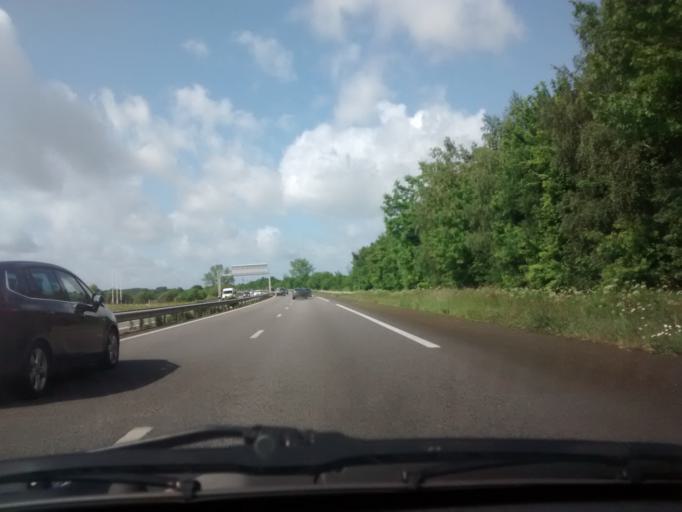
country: FR
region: Brittany
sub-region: Departement d'Ille-et-Vilaine
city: Le Rheu
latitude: 48.0907
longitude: -1.7760
